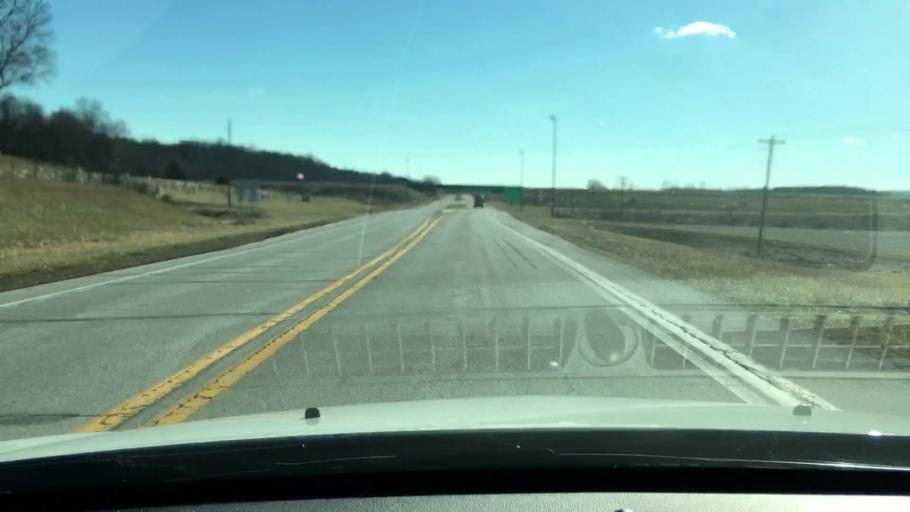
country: US
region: Illinois
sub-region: Scott County
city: Winchester
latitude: 39.6896
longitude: -90.5712
